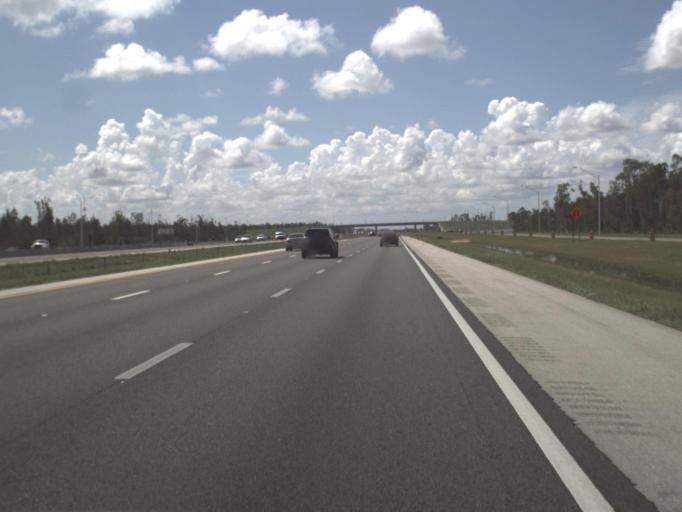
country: US
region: Florida
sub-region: Lee County
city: Three Oaks
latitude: 26.5210
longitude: -81.7949
